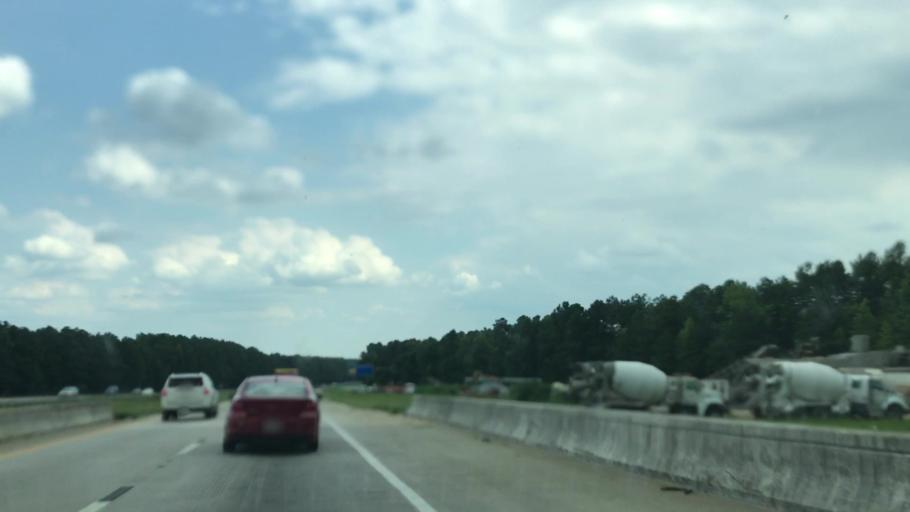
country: US
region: South Carolina
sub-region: Richland County
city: Blythewood
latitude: 34.3079
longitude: -81.0003
